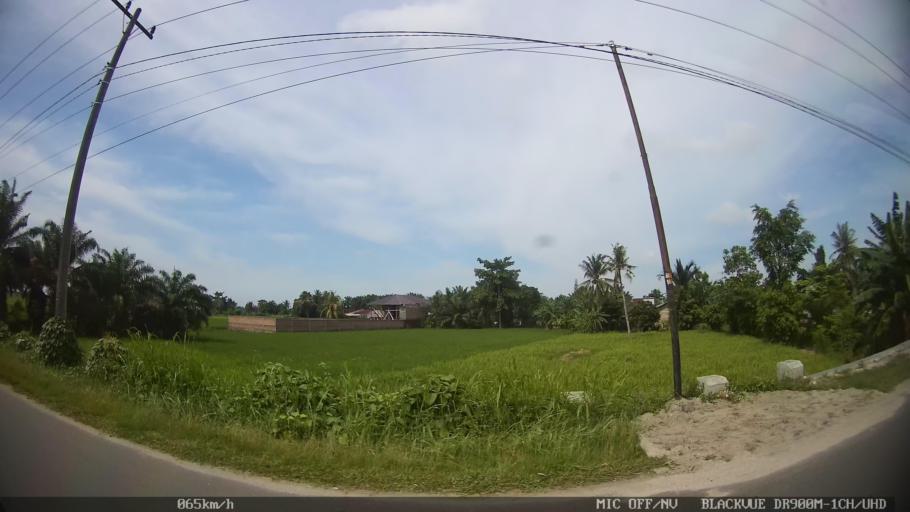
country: ID
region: North Sumatra
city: Percut
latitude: 3.6132
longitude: 98.8441
